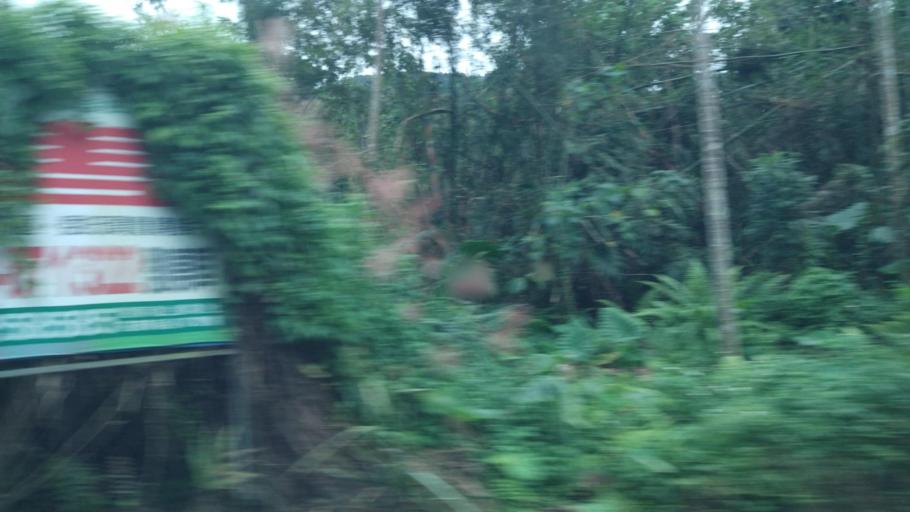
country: TW
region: Taiwan
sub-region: Hualien
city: Hualian
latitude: 23.9204
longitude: 121.5032
